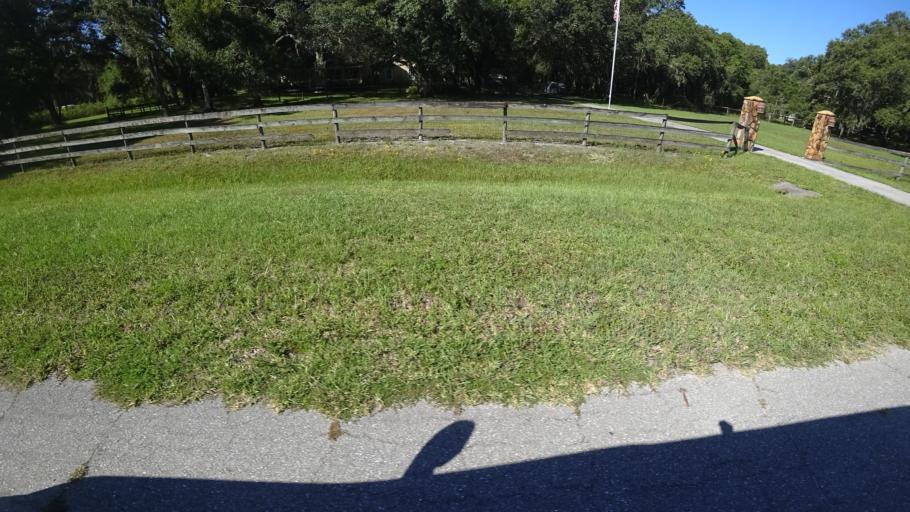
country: US
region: Florida
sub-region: Sarasota County
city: Lake Sarasota
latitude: 27.2870
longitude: -82.2281
